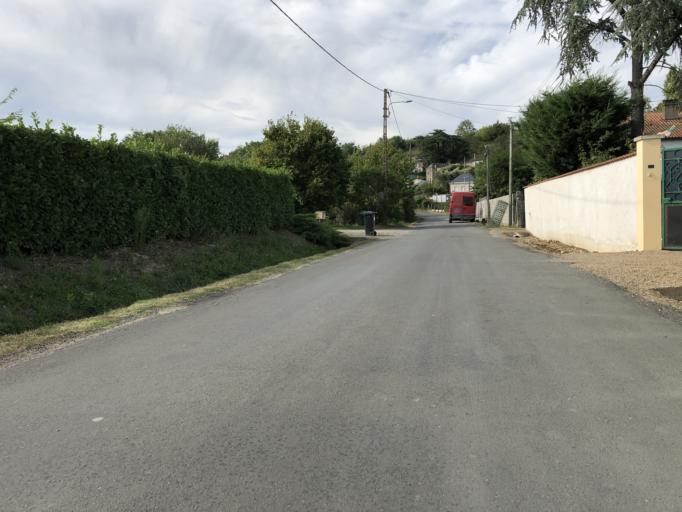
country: FR
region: Pays de la Loire
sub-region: Departement de la Sarthe
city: Chateau-du-Loir
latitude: 47.6812
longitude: 0.4268
